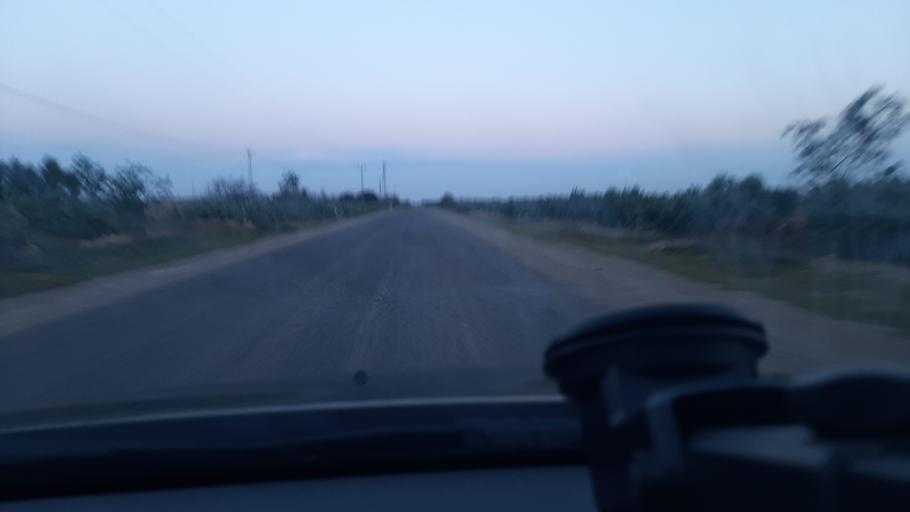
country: TN
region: Al Mahdiyah
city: Shurban
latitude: 35.0174
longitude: 10.4529
